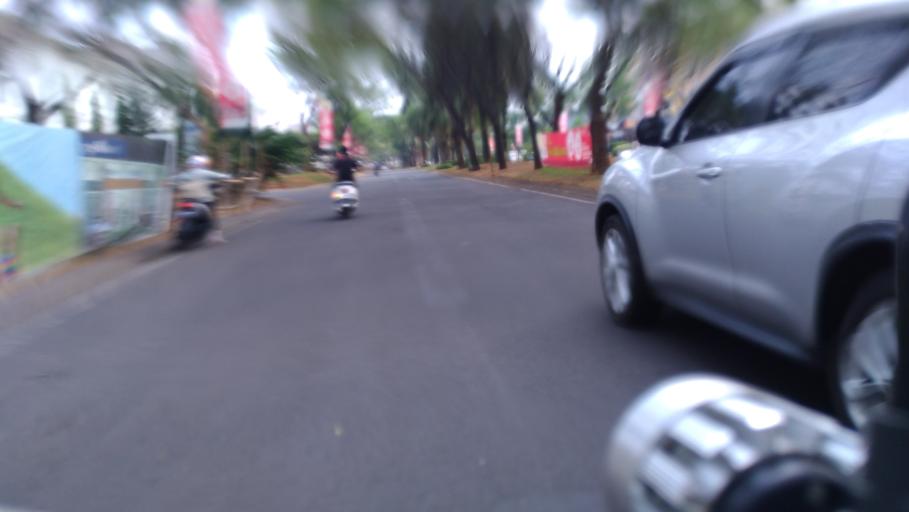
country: ID
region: West Java
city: Cileungsir
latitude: -6.3919
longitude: 106.9473
